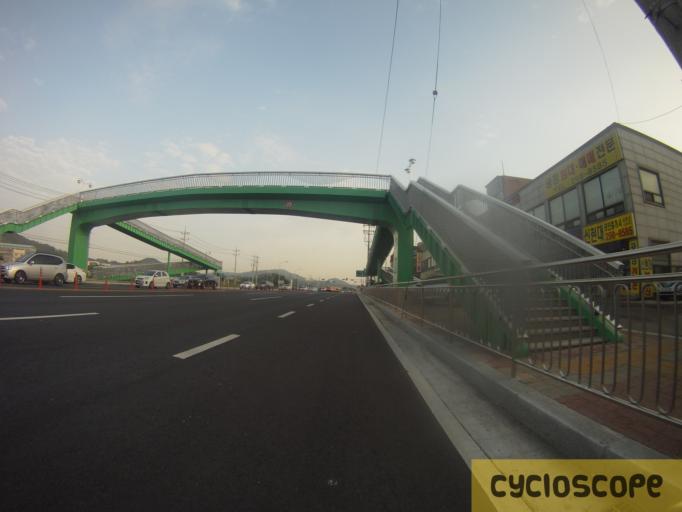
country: KR
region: Gyeonggi-do
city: Suwon-si
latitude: 37.1926
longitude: 126.9391
